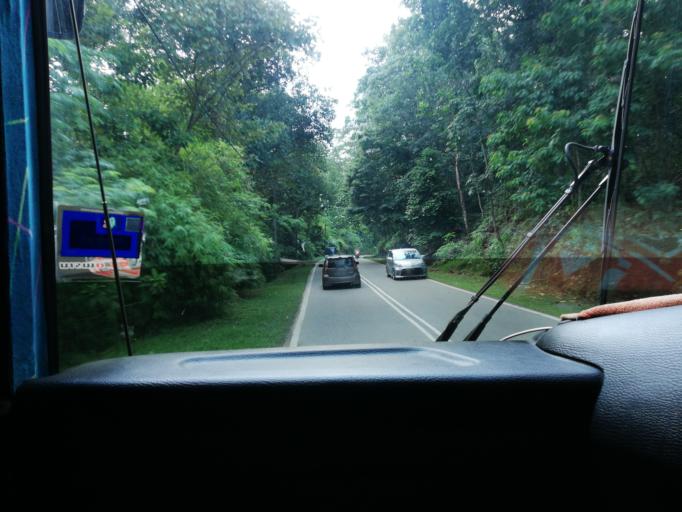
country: MY
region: Kedah
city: Kulim
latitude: 5.3038
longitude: 100.6181
